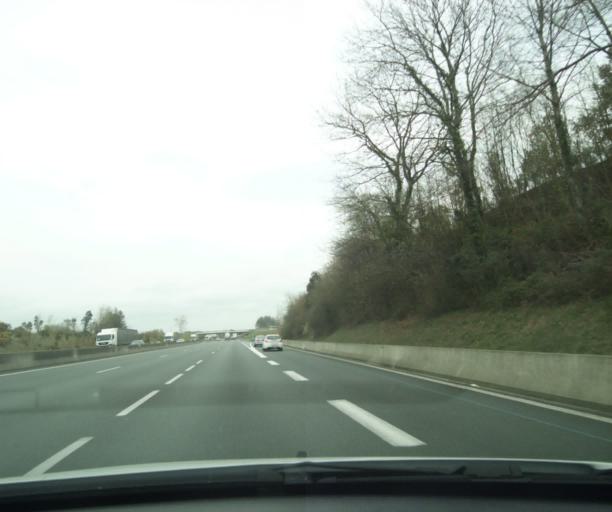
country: FR
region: Aquitaine
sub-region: Departement des Pyrenees-Atlantiques
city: Anglet
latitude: 43.4612
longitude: -1.5042
